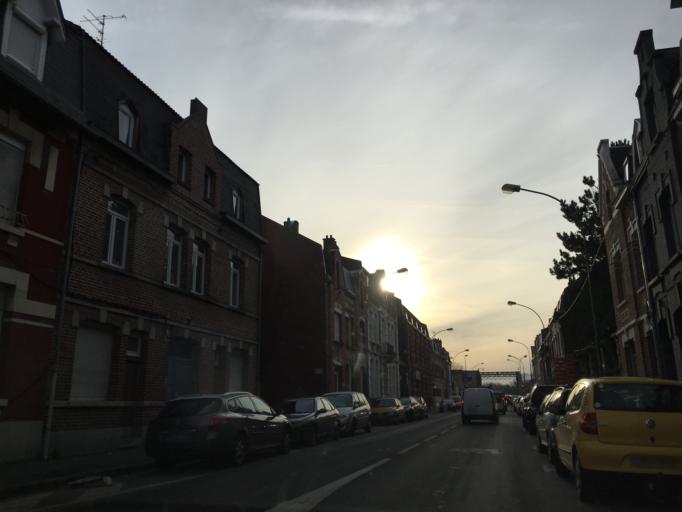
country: FR
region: Nord-Pas-de-Calais
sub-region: Departement du Pas-de-Calais
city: Arras
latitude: 50.2900
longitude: 2.7844
